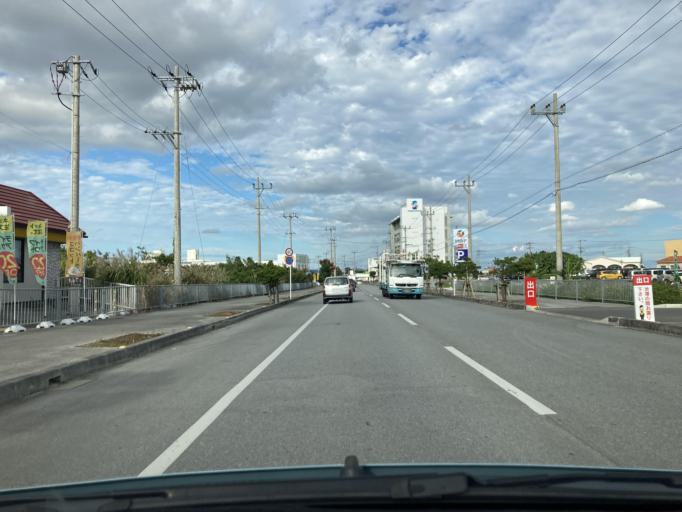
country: JP
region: Okinawa
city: Okinawa
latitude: 26.3682
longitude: 127.8254
